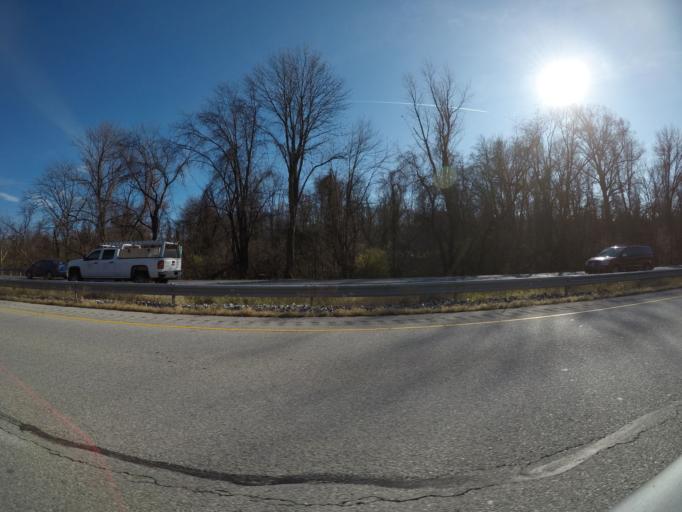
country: US
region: Pennsylvania
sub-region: Chester County
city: Caln
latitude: 40.0031
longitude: -75.8004
